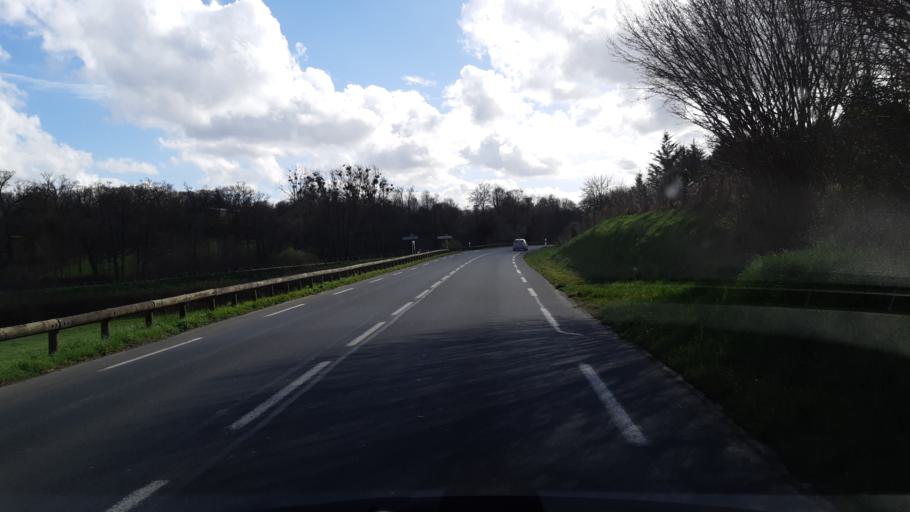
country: FR
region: Lower Normandy
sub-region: Departement de la Manche
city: Agneaux
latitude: 49.0828
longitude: -1.1174
